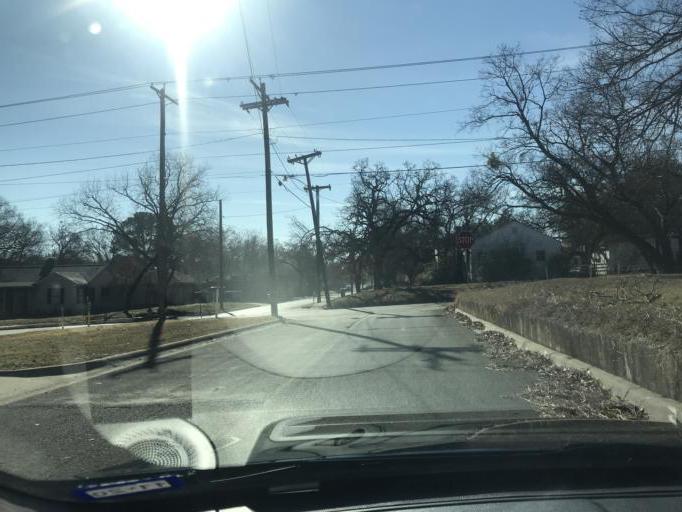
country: US
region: Texas
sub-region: Denton County
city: Denton
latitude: 33.2191
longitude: -97.1540
